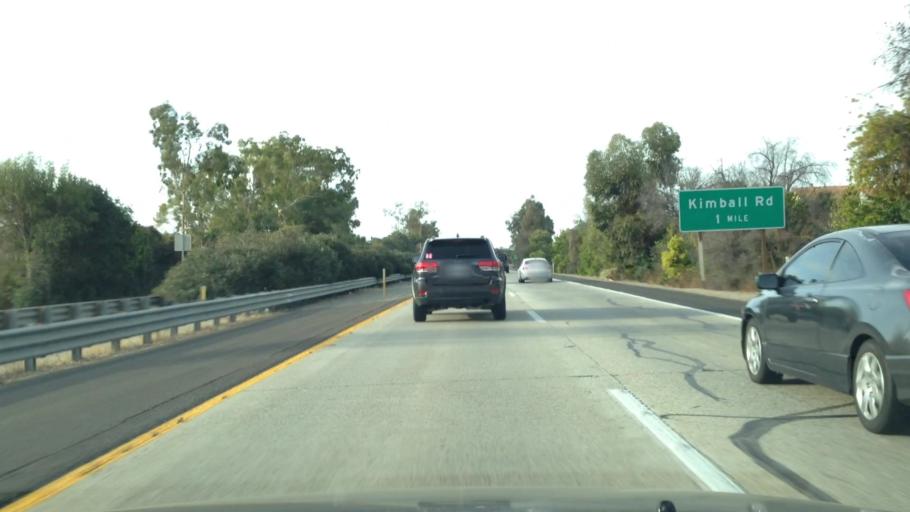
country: US
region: California
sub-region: Ventura County
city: Saticoy
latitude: 34.2796
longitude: -119.1735
